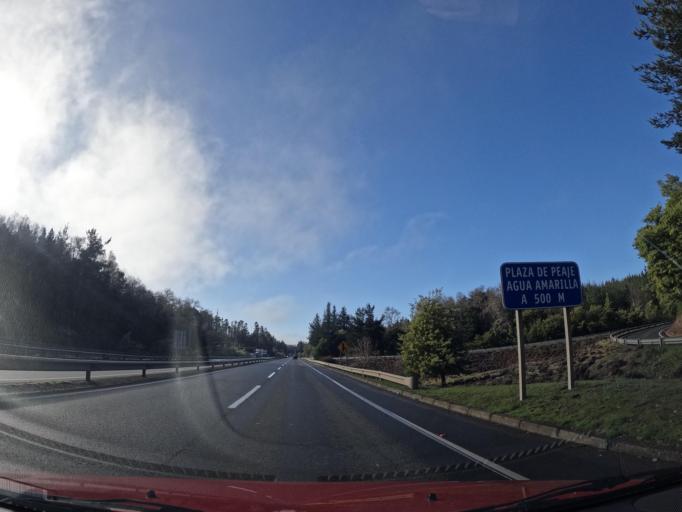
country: CL
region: Biobio
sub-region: Provincia de Concepcion
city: Penco
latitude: -36.7300
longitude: -72.8648
